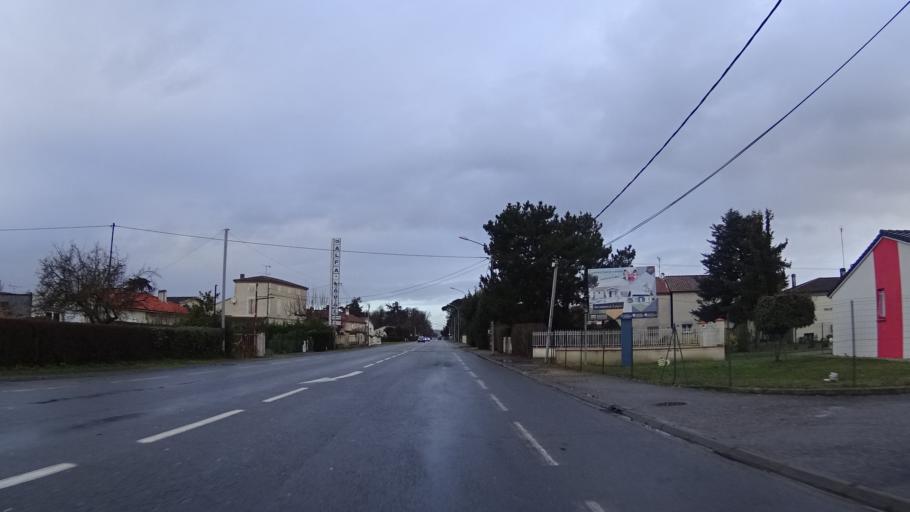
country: FR
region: Aquitaine
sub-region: Departement du Lot-et-Garonne
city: Boe
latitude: 44.1716
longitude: 0.6082
